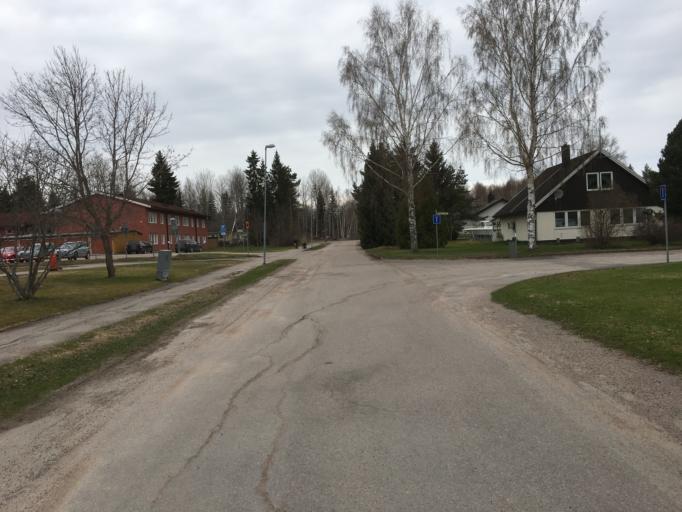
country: SE
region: Gaevleborg
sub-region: Hofors Kommun
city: Hofors
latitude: 60.5139
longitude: 16.4705
